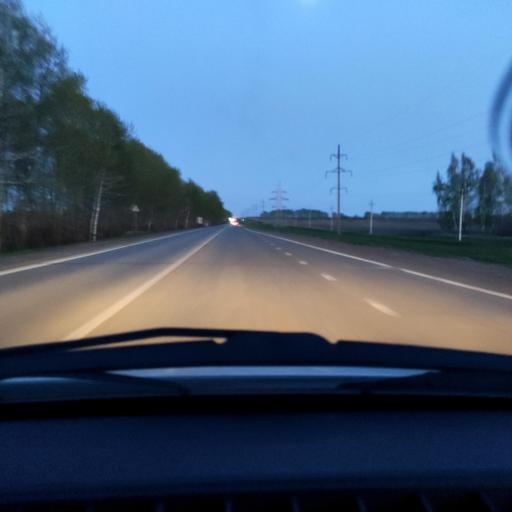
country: RU
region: Bashkortostan
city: Mikhaylovka
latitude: 54.8622
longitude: 55.7531
